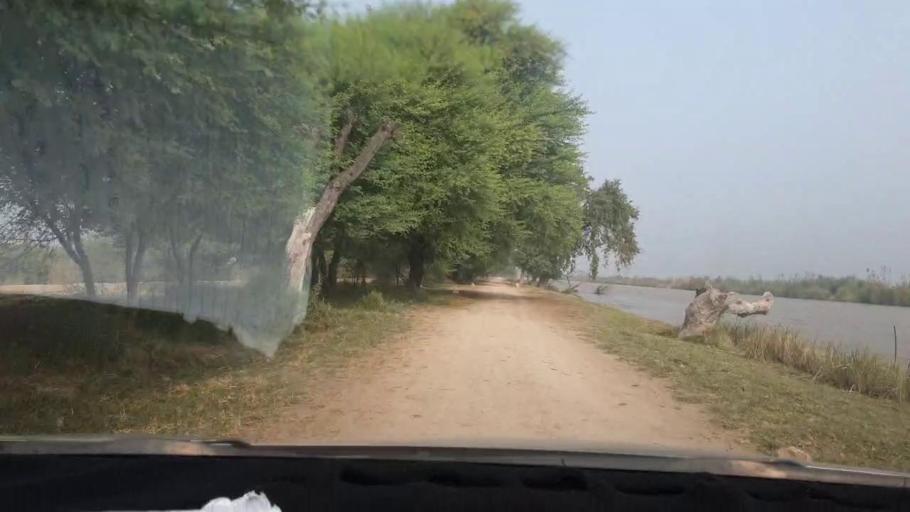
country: PK
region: Sindh
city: Tando Adam
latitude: 25.6785
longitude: 68.5570
